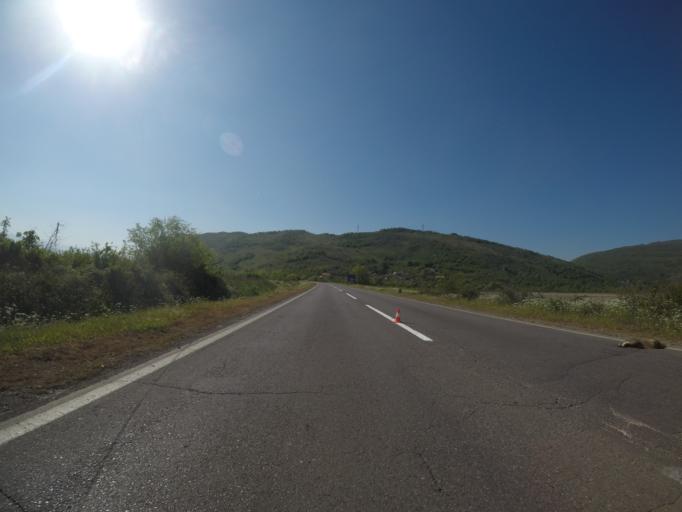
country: ME
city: Spuz
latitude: 42.4641
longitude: 19.1756
